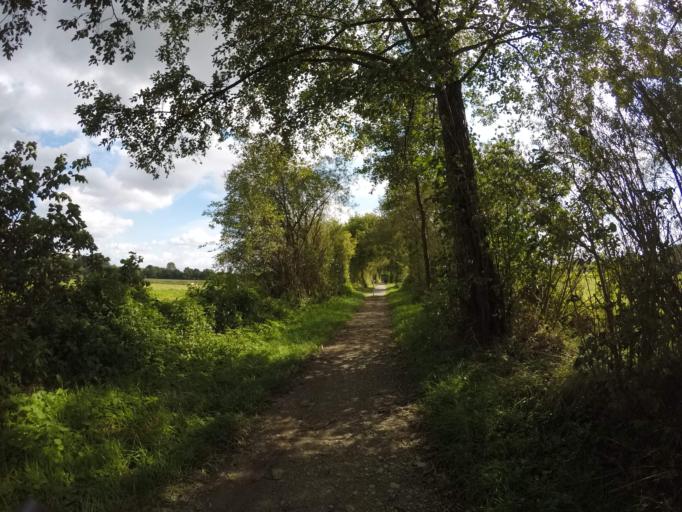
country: DE
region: North Rhine-Westphalia
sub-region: Regierungsbezirk Detmold
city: Hiddenhausen
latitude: 52.1405
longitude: 8.6277
